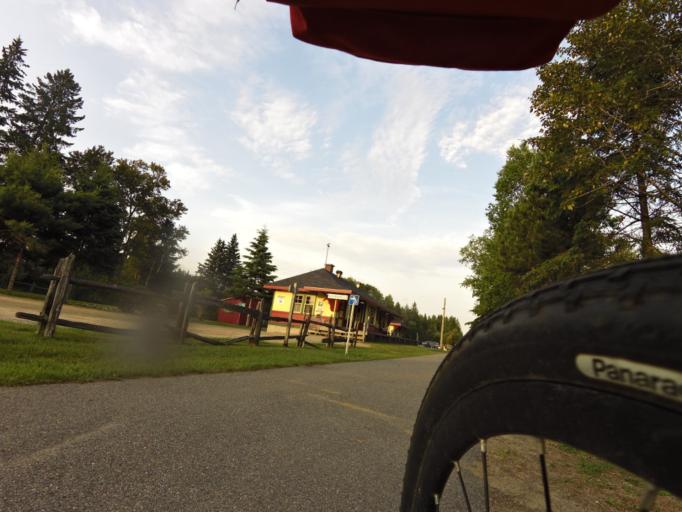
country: CA
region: Quebec
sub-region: Laurentides
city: Riviere-Rouge
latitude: 46.3943
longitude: -75.0282
